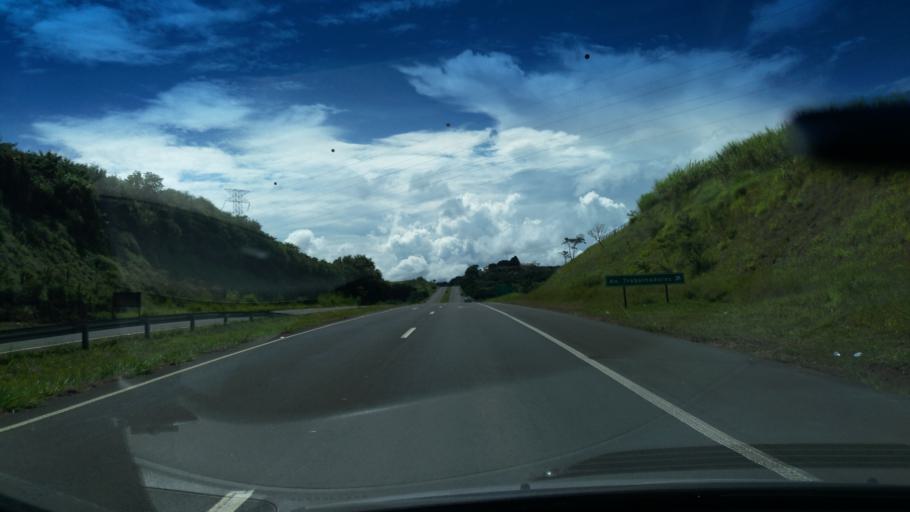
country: BR
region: Sao Paulo
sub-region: Santo Antonio Do Jardim
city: Espirito Santo do Pinhal
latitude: -22.1831
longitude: -46.7612
